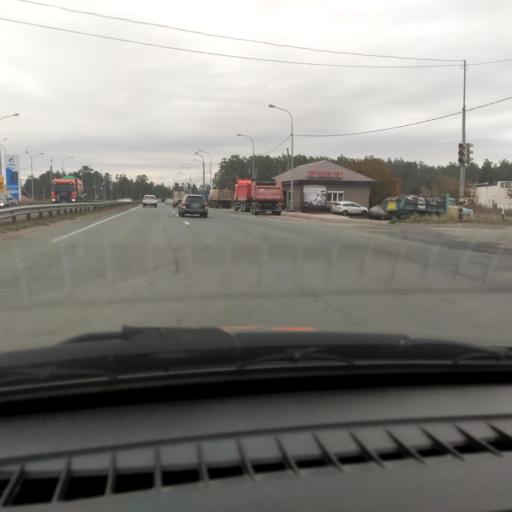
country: RU
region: Samara
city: Zhigulevsk
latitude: 53.5420
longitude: 49.5143
